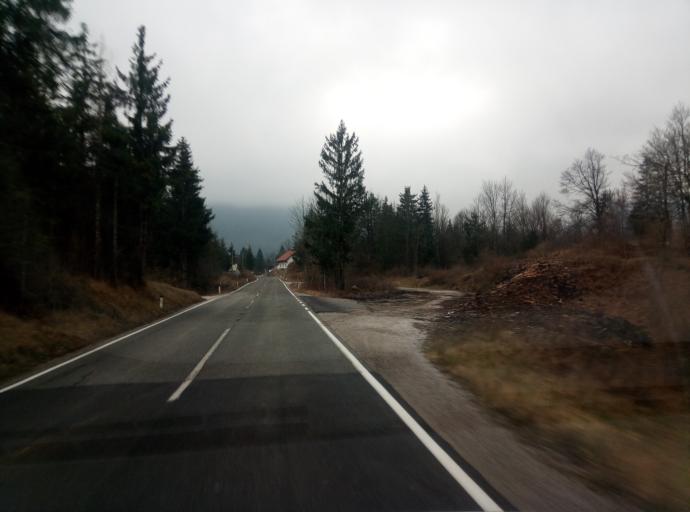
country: SI
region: Idrija
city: Idrija
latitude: 45.9352
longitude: 14.0678
